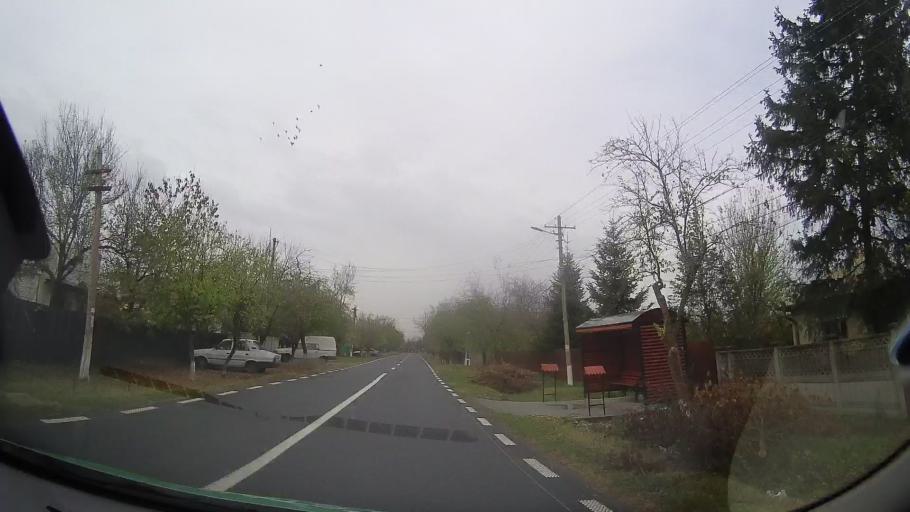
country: RO
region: Ilfov
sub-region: Comuna Nuci
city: Nuci
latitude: 44.7208
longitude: 26.2956
